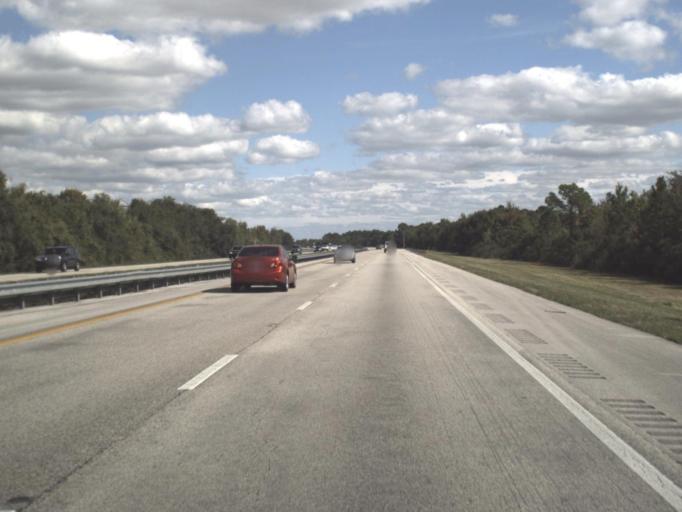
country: US
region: Florida
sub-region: Indian River County
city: Fellsmere
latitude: 27.5615
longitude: -80.7762
